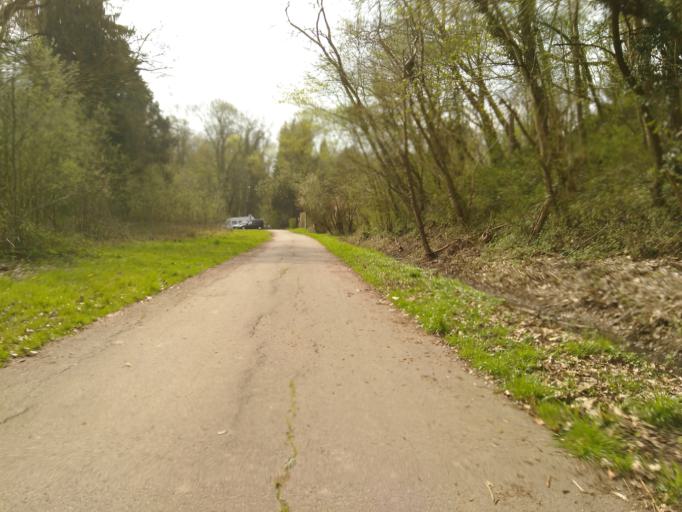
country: BE
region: Wallonia
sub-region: Province du Brabant Wallon
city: Chaumont-Gistoux
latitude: 50.6866
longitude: 4.6983
